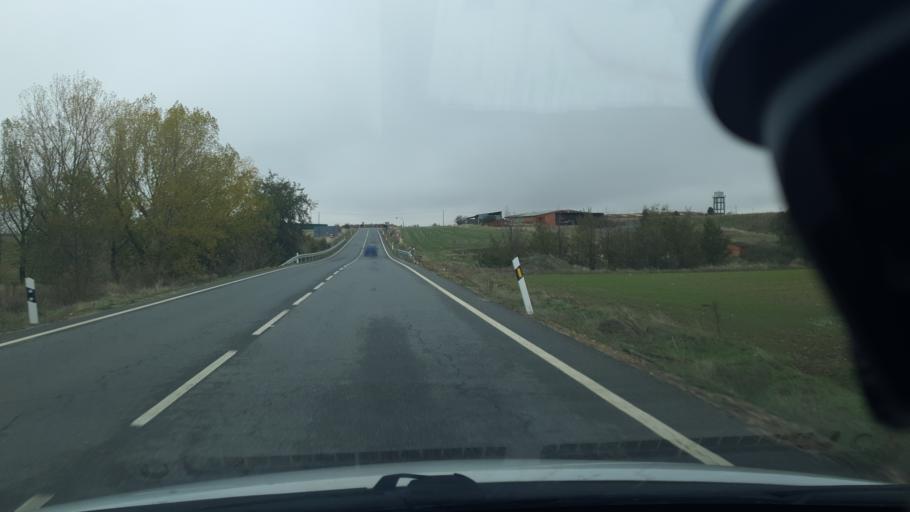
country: ES
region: Castille and Leon
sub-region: Provincia de Segovia
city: Turegano
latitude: 41.1526
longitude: -4.0163
